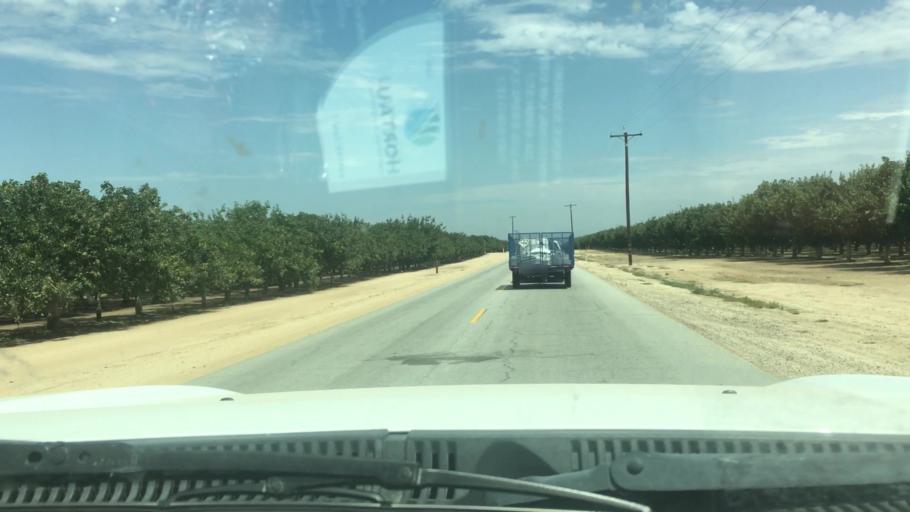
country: US
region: California
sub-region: Kern County
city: McFarland
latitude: 35.5960
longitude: -119.1510
